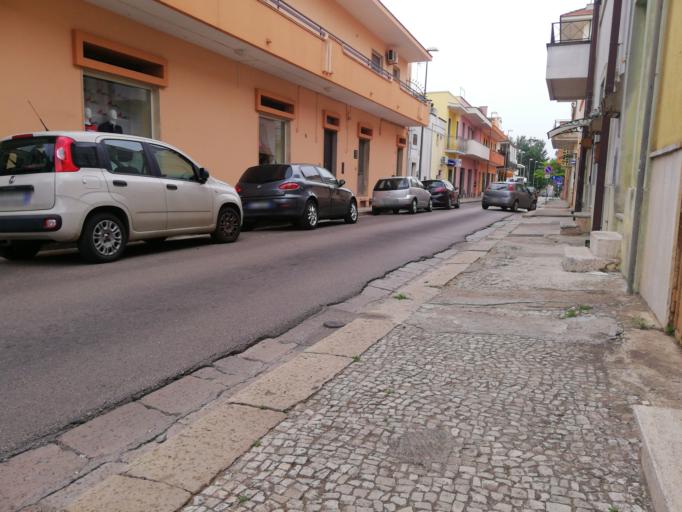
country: IT
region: Apulia
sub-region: Provincia di Lecce
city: Taurisano
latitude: 39.9572
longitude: 18.2120
